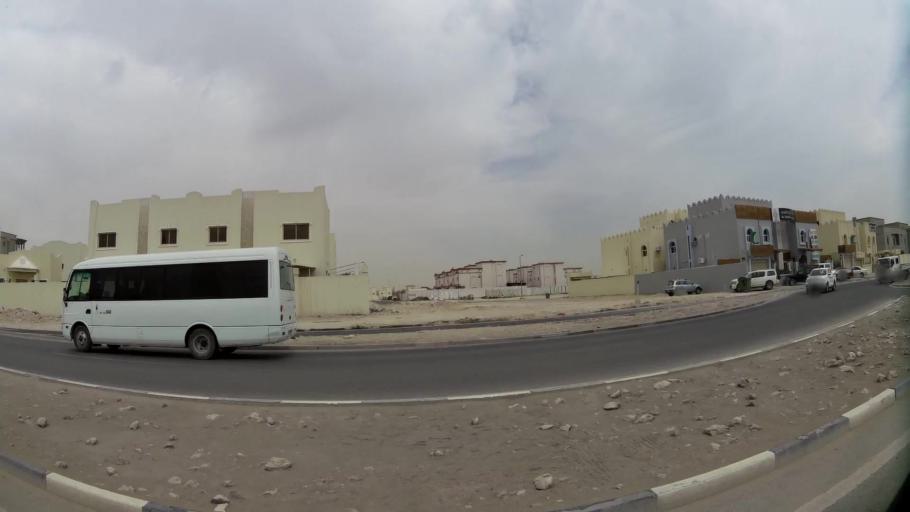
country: QA
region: Baladiyat ad Dawhah
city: Doha
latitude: 25.2187
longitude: 51.4775
